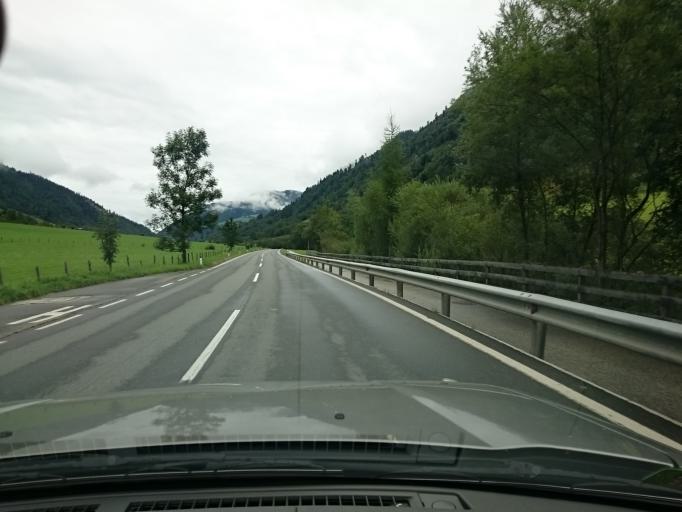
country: AT
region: Salzburg
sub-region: Politischer Bezirk Zell am See
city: Bruck an der Grossglocknerstrasse
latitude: 47.2447
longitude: 12.8270
